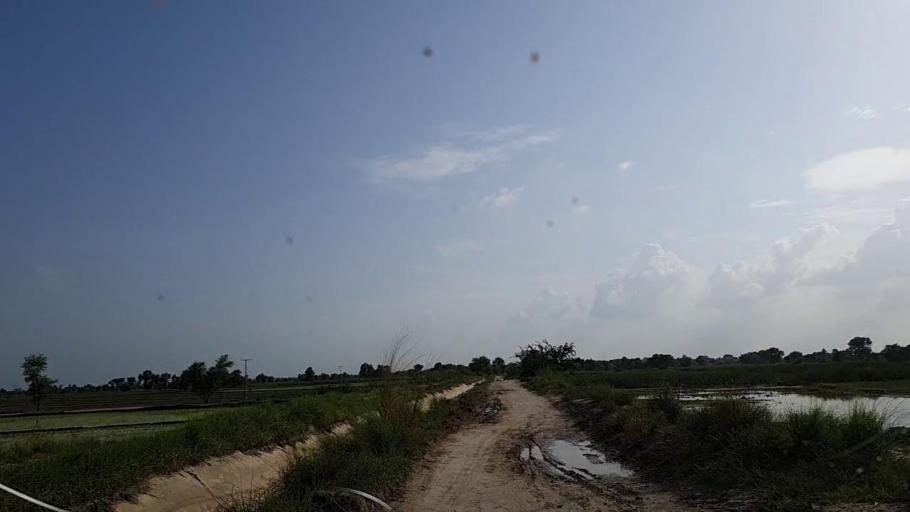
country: PK
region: Sindh
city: Bhiria
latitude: 26.8664
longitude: 68.2552
